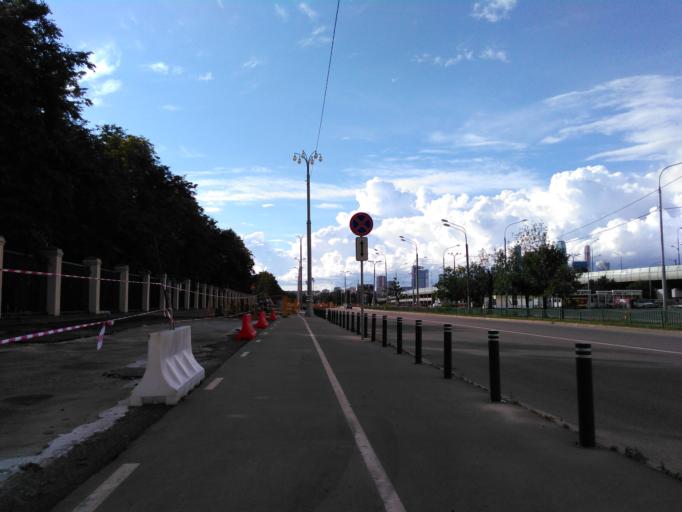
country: RU
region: Moscow
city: Luzhniki
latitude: 55.7204
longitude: 37.5555
